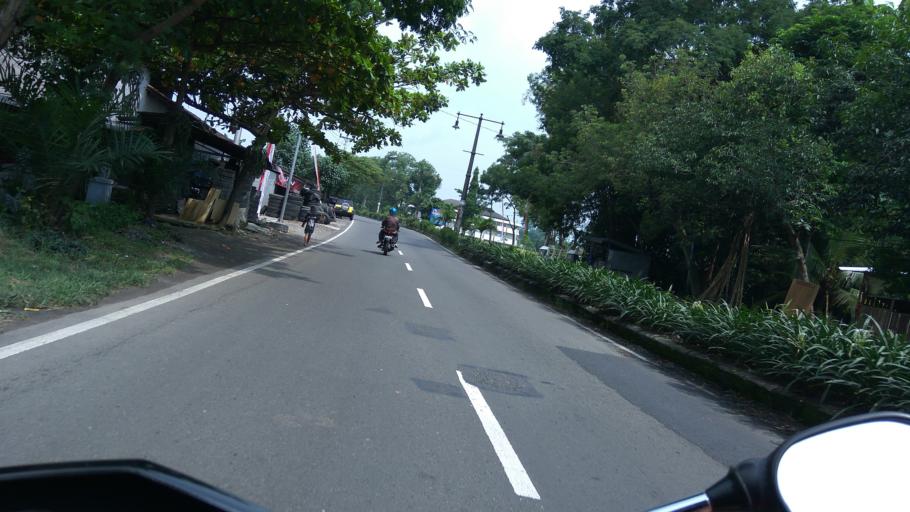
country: ID
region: Central Java
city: Jaten
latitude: -7.5853
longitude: 110.9150
